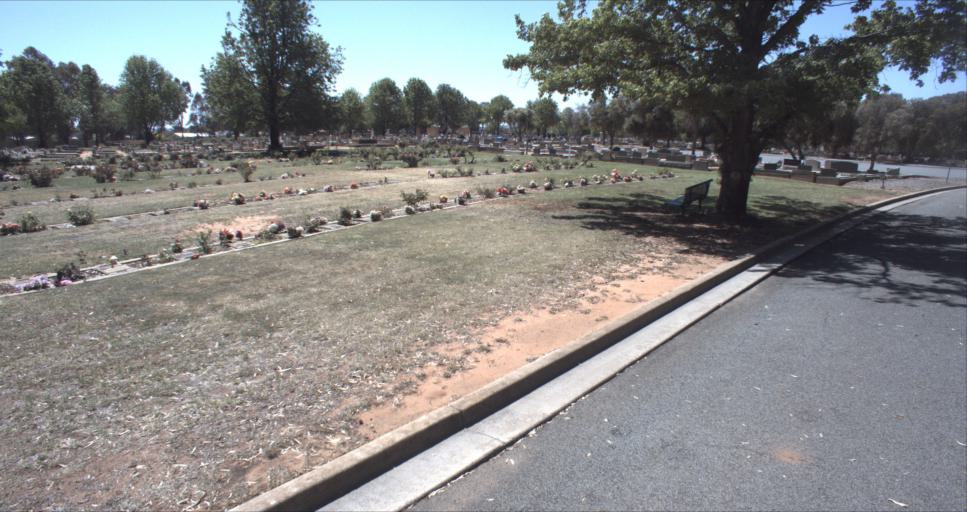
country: AU
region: New South Wales
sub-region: Leeton
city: Leeton
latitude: -34.5328
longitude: 146.3973
